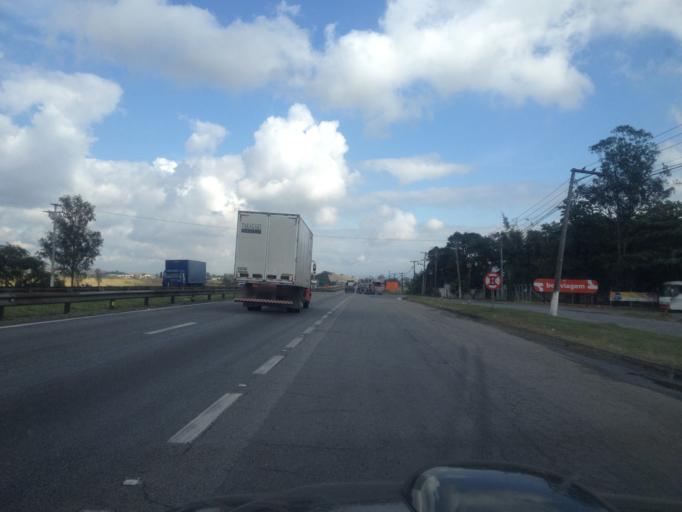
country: BR
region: Rio de Janeiro
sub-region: Porto Real
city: Porto Real
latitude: -22.4525
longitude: -44.3590
